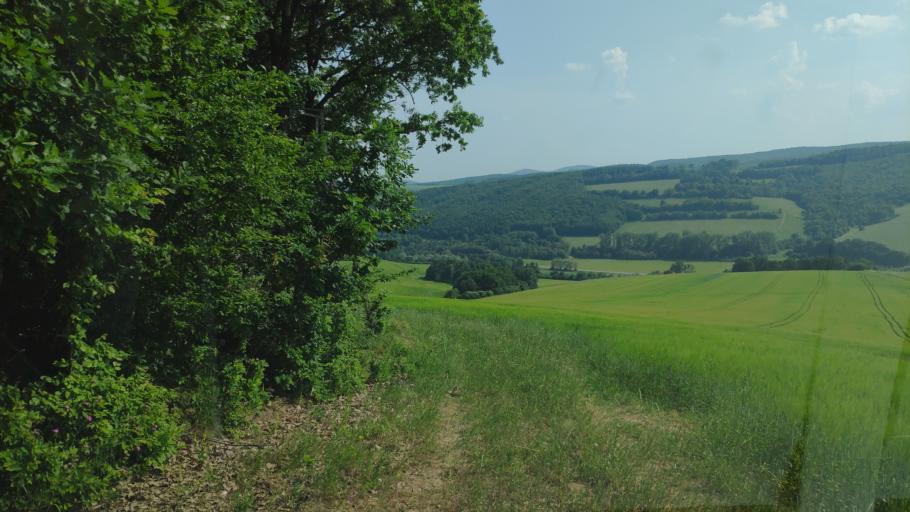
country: SK
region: Presovsky
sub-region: Okres Presov
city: Presov
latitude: 48.9653
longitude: 21.1519
